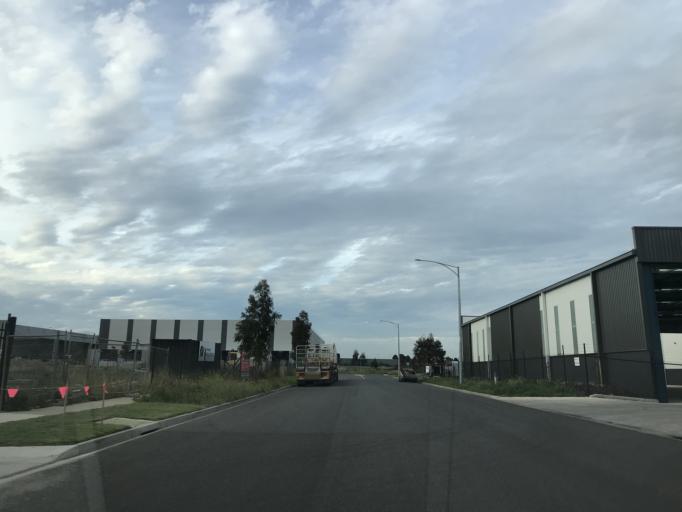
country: AU
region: Victoria
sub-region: Brimbank
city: Derrimut
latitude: -37.8014
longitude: 144.7632
